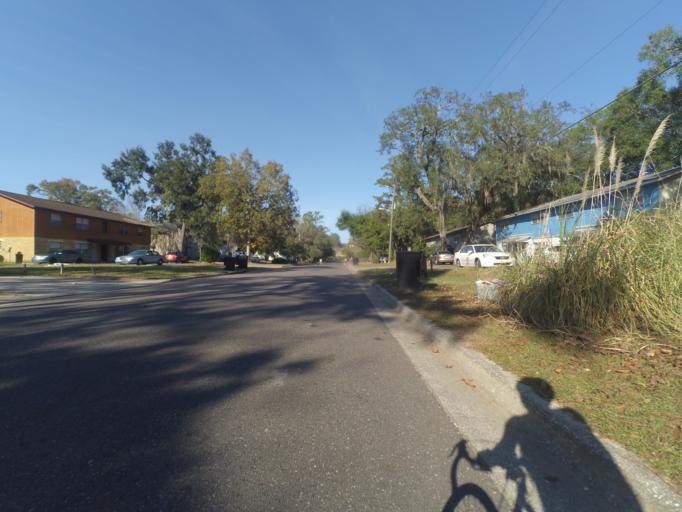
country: US
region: Florida
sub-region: Alachua County
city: Gainesville
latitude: 29.6178
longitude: -82.3655
